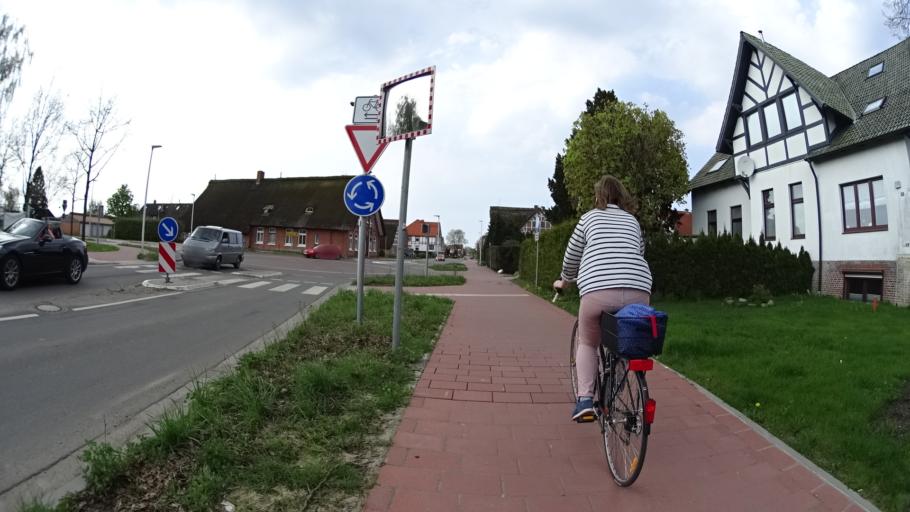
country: DE
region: Lower Saxony
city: Jork
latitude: 53.5311
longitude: 9.6886
